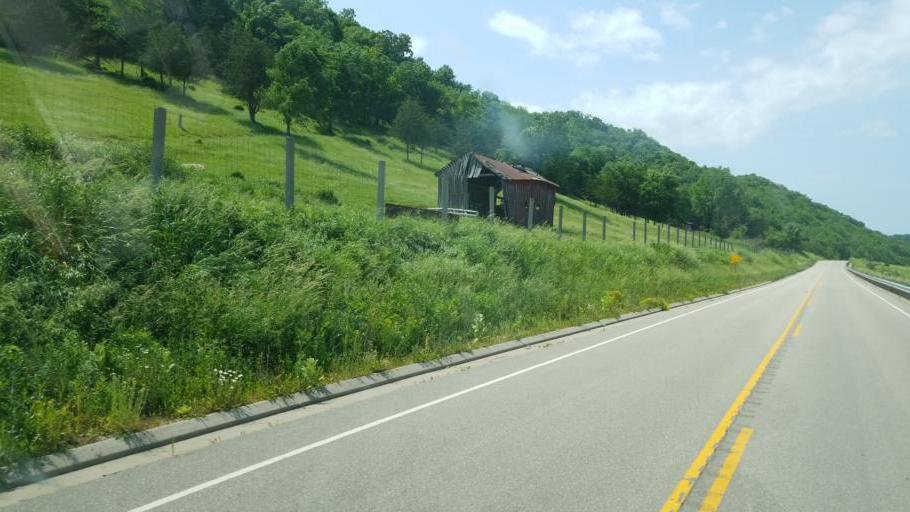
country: US
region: Wisconsin
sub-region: Vernon County
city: Viroqua
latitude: 43.5155
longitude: -90.6614
